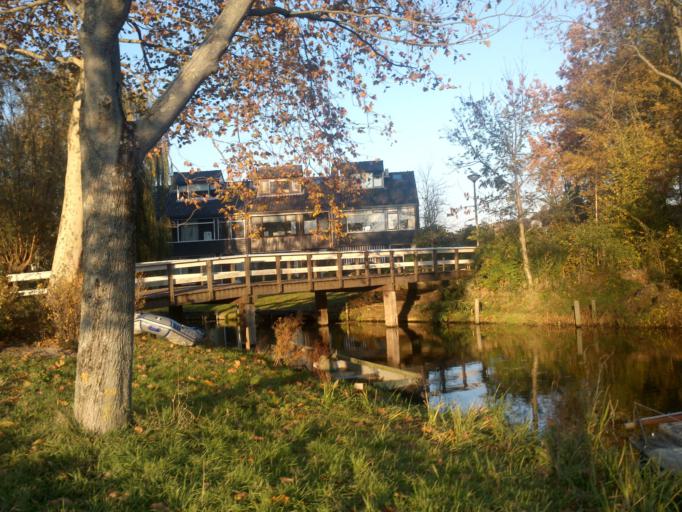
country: NL
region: South Holland
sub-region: Gemeente Teylingen
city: Sassenheim
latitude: 52.2182
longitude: 4.5196
